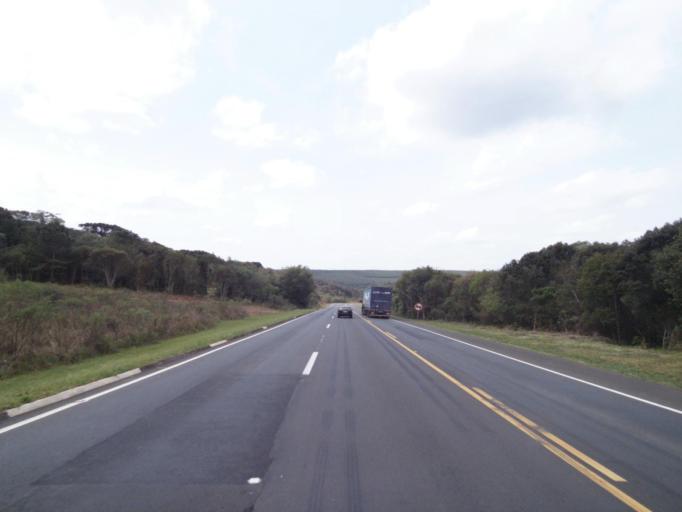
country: BR
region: Parana
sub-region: Irati
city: Irati
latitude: -25.4571
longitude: -50.4587
